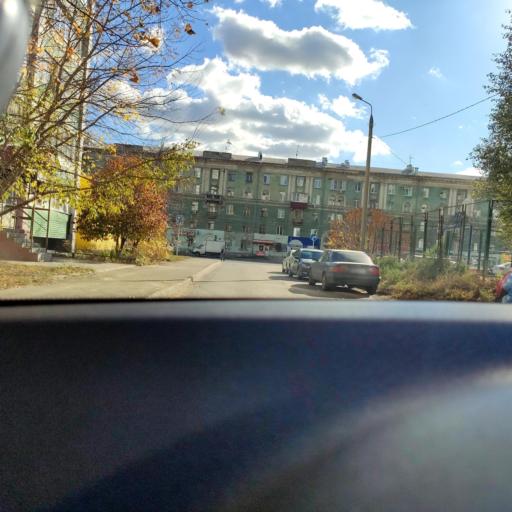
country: RU
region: Samara
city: Petra-Dubrava
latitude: 53.2258
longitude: 50.2748
